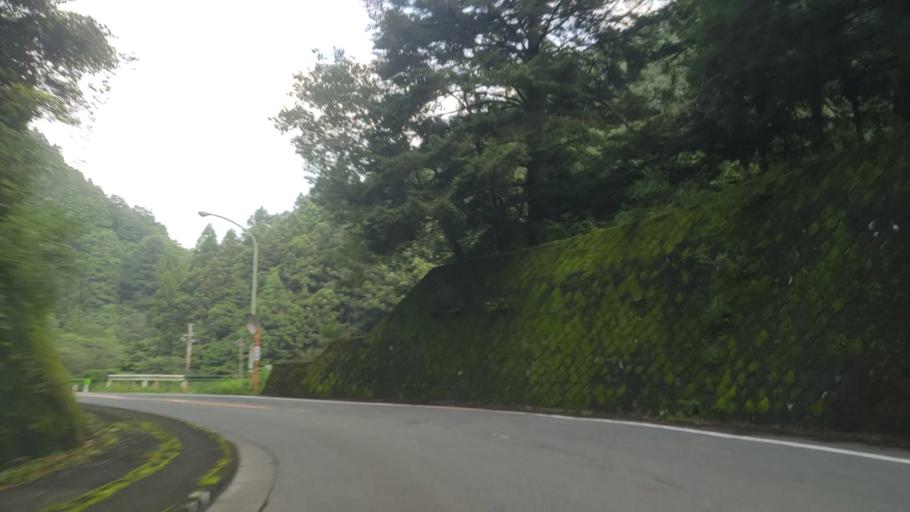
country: JP
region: Tokyo
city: Ome
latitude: 35.8358
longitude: 139.2185
